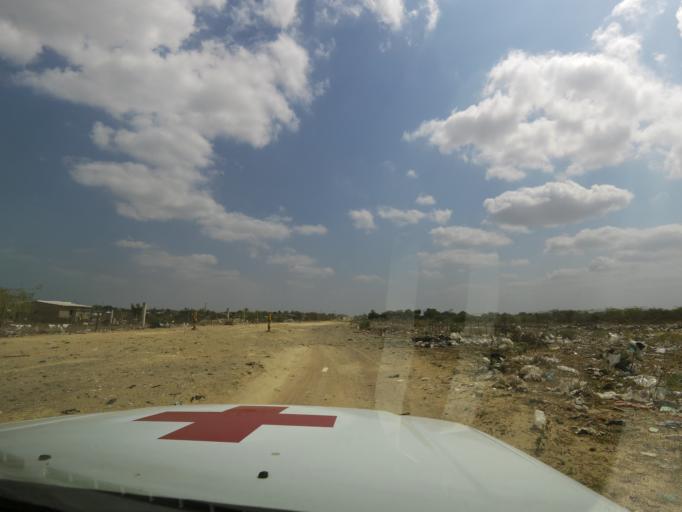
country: CO
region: La Guajira
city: Riohacha
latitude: 11.5214
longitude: -72.9206
